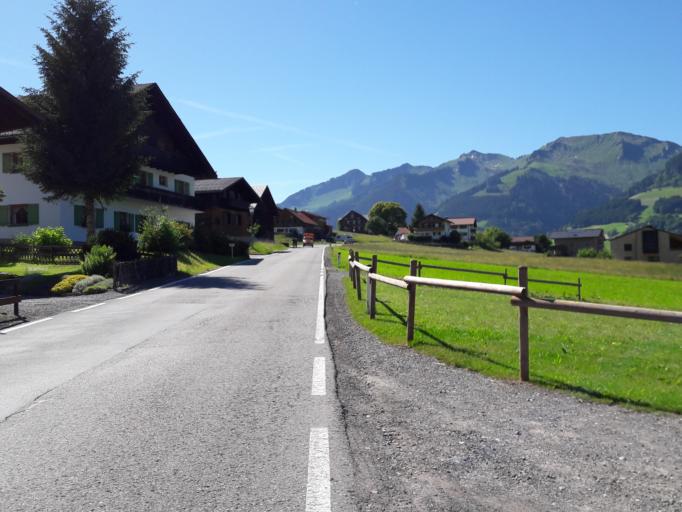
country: AT
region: Vorarlberg
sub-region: Politischer Bezirk Bludenz
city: Raggal
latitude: 47.2108
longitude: 9.8436
